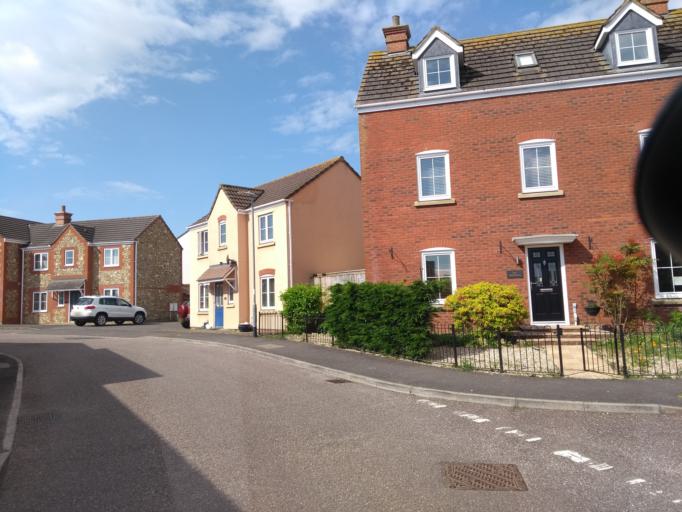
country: GB
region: England
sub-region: Somerset
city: Chard
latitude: 50.8691
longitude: -2.9703
